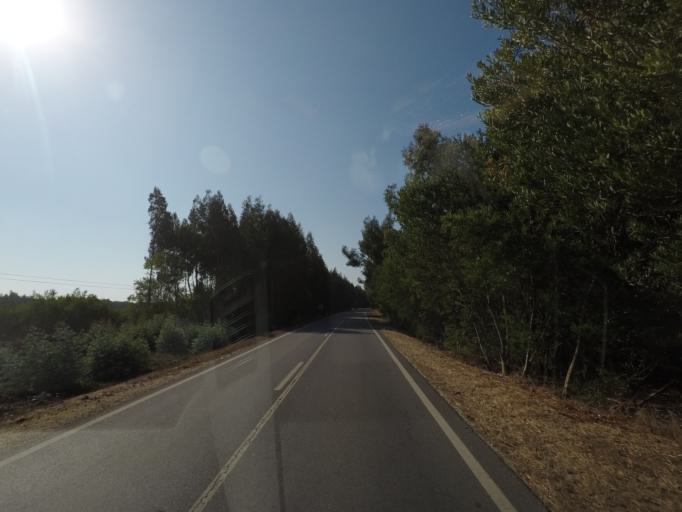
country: PT
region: Beja
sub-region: Odemira
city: Vila Nova de Milfontes
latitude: 37.6734
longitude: -8.7554
